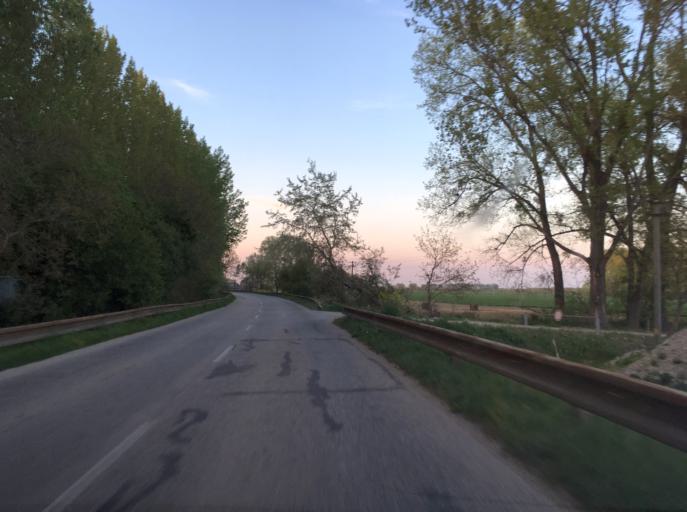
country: SK
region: Nitriansky
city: Kolarovo
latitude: 47.9223
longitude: 18.0148
